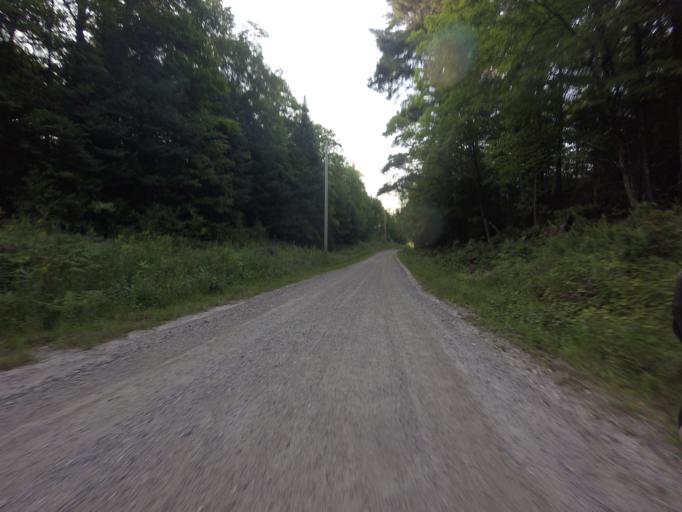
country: CA
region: Ontario
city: Renfrew
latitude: 45.0543
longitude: -76.7500
